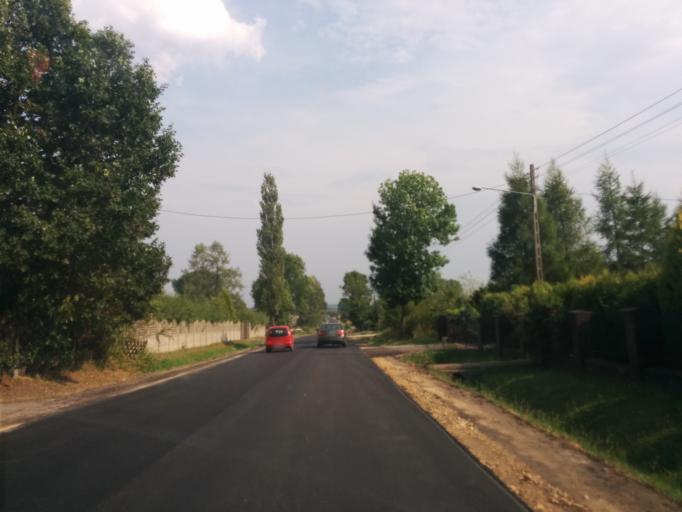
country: PL
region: Silesian Voivodeship
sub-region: Powiat myszkowski
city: Zarki
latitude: 50.6056
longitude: 19.4125
